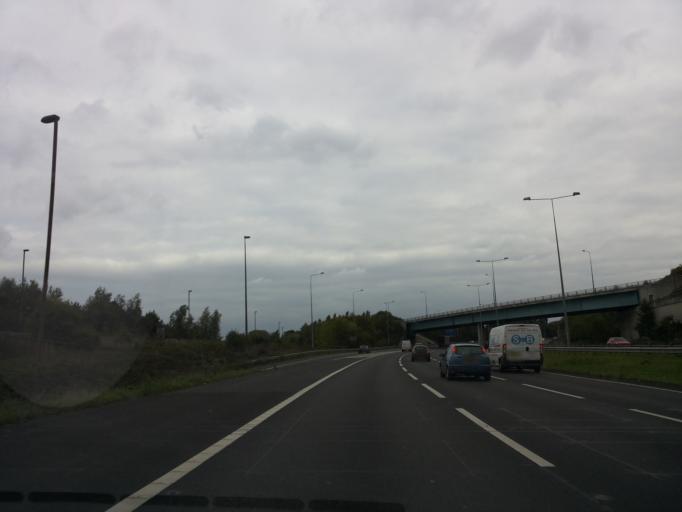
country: GB
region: England
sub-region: Medway
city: Cuxton
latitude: 51.3994
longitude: 0.4482
